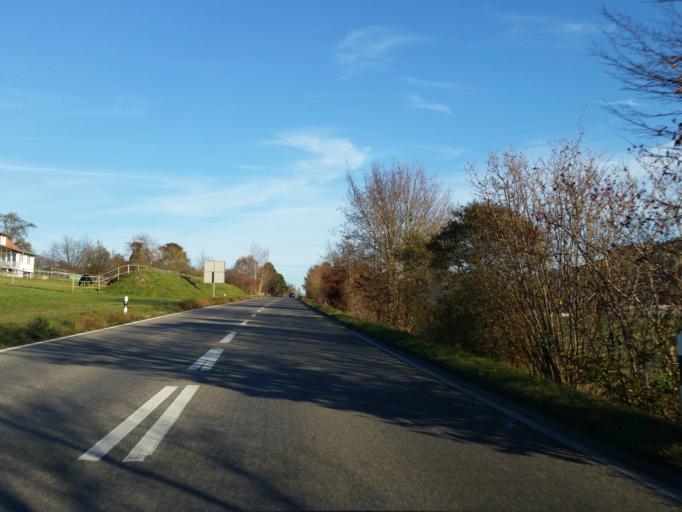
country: CH
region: Thurgau
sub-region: Frauenfeld District
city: Diessenhofen
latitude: 47.6793
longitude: 8.7548
